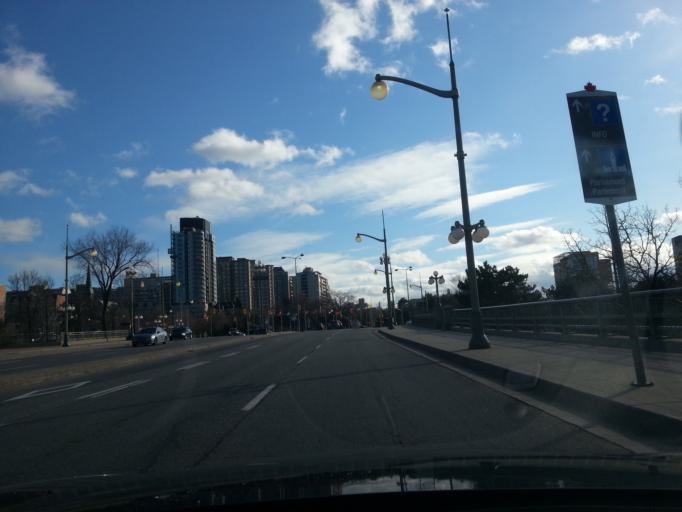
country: CA
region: Ontario
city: Ottawa
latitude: 45.4202
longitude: -75.7124
